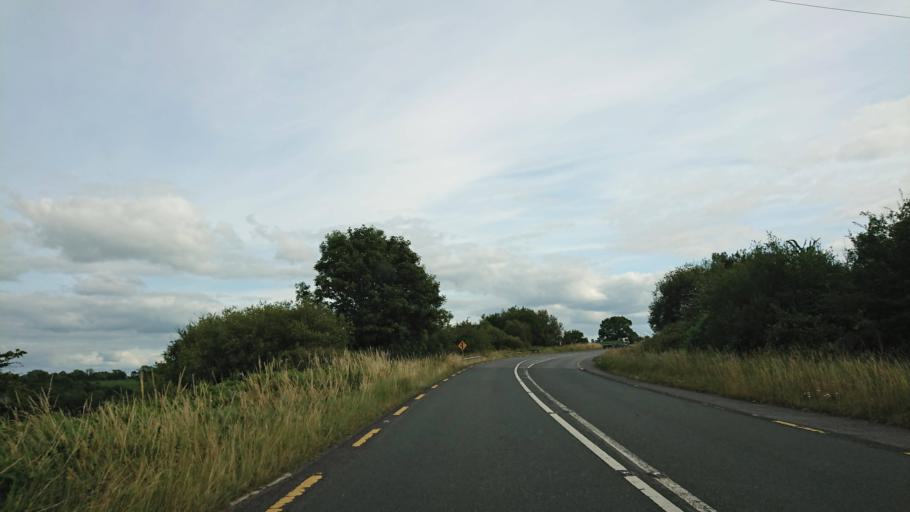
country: IE
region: Connaught
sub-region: County Leitrim
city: Carrick-on-Shannon
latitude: 53.9781
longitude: -8.0609
